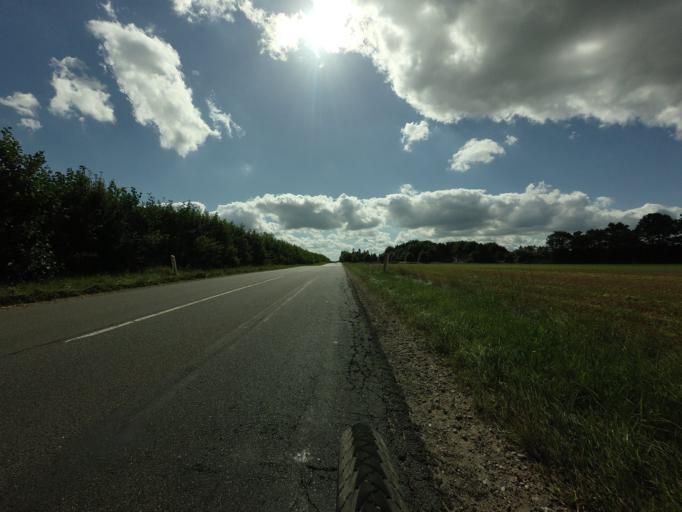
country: DK
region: Central Jutland
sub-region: Ikast-Brande Kommune
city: Brande
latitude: 55.9761
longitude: 9.1455
